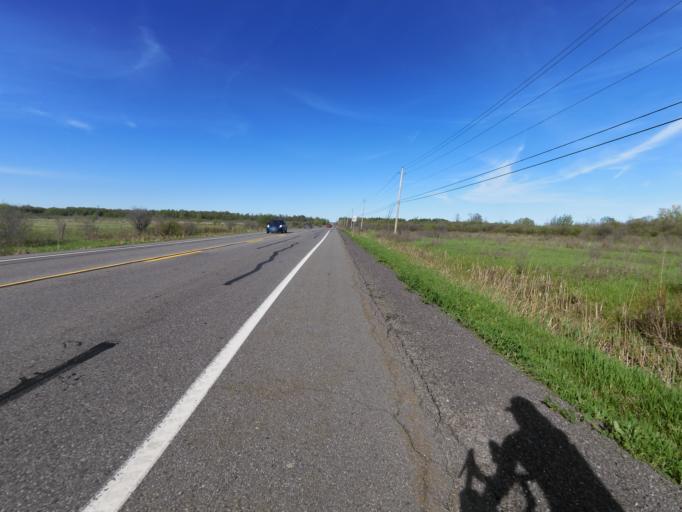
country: CA
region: Ontario
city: Ottawa
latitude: 45.3004
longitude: -75.6704
